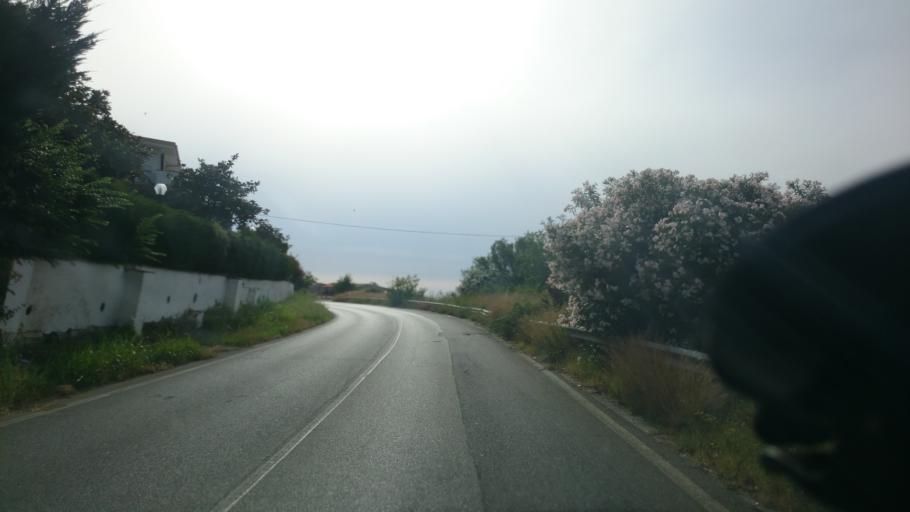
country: IT
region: Calabria
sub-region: Provincia di Vibo-Valentia
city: Parghelia
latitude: 38.6897
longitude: 15.9473
